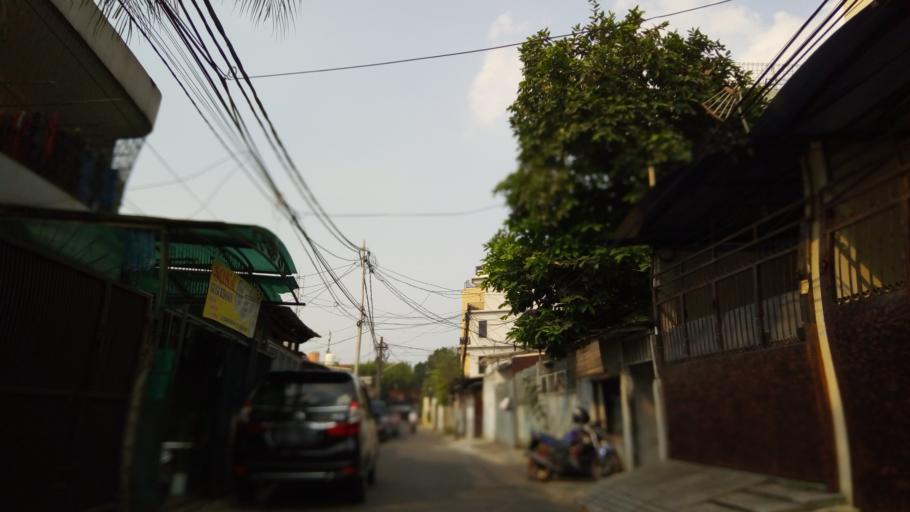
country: ID
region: Jakarta Raya
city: Jakarta
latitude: -6.1796
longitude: 106.8445
